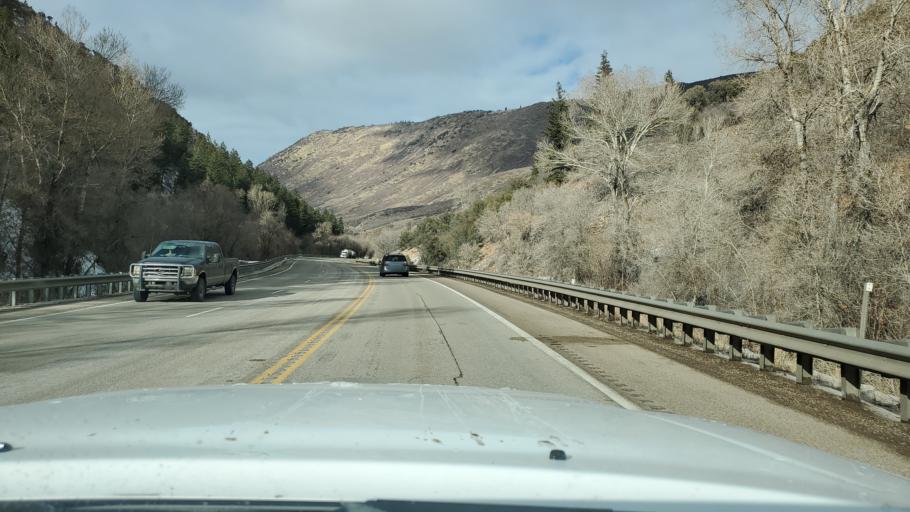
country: US
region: Utah
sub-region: Wasatch County
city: Heber
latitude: 40.3958
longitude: -111.3026
